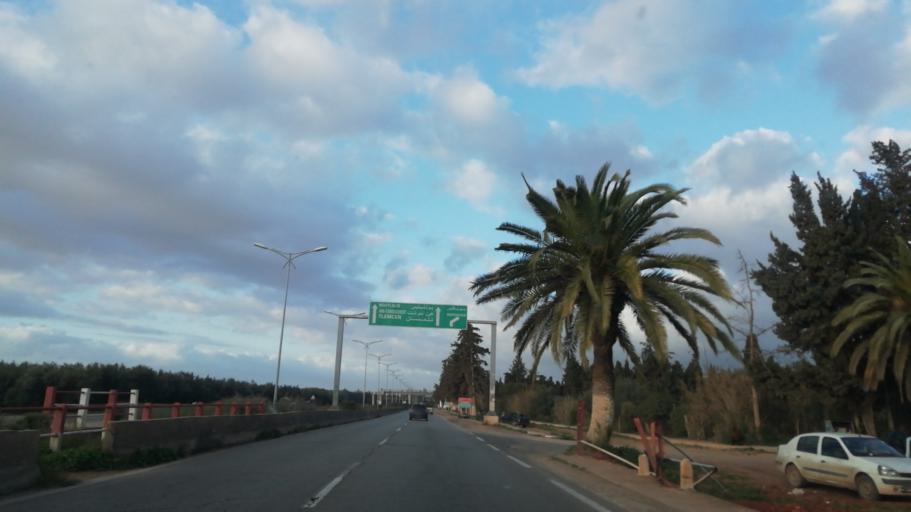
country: DZ
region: Oran
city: Bou Tlelis
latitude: 35.5890
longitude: -0.8041
